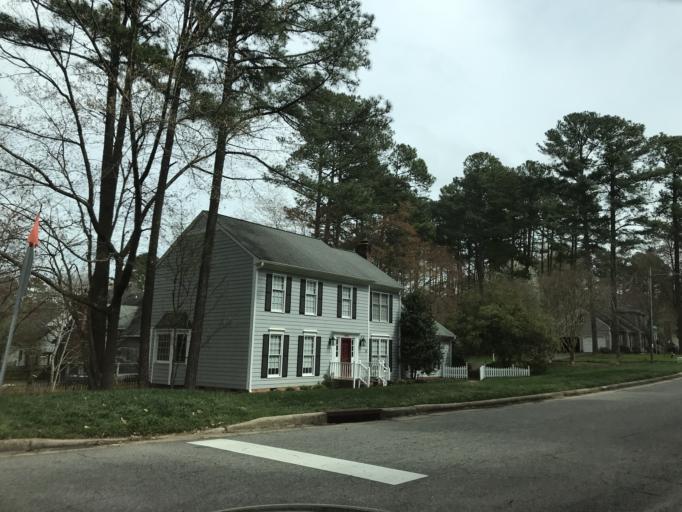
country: US
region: North Carolina
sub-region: Wake County
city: West Raleigh
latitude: 35.8869
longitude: -78.6720
